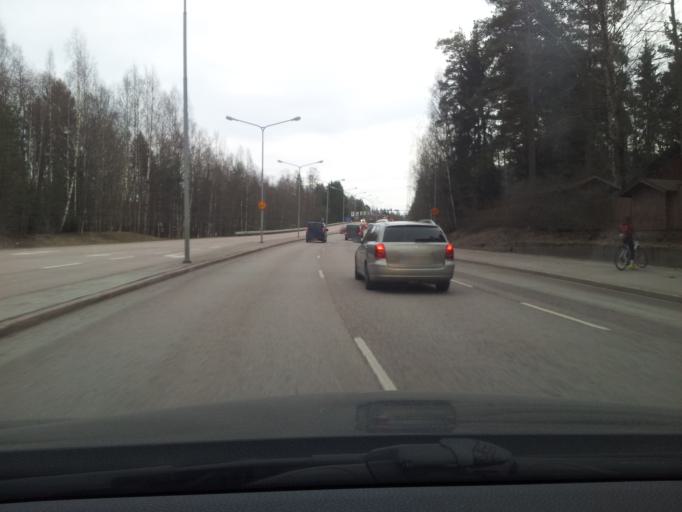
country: FI
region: Uusimaa
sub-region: Helsinki
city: Espoo
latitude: 60.1465
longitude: 24.6717
